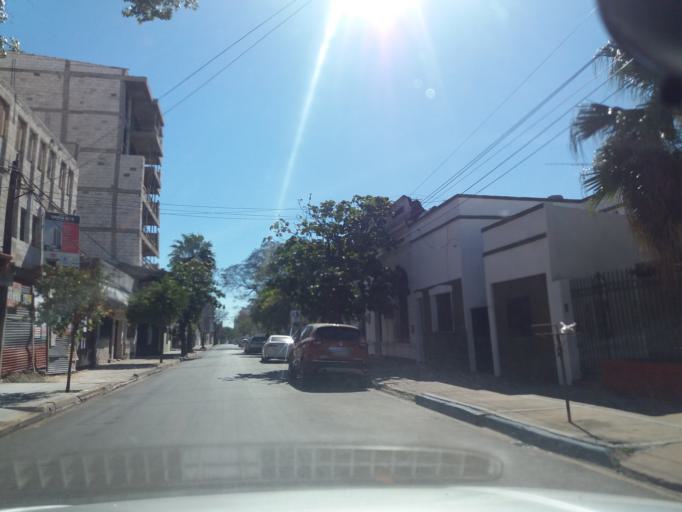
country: AR
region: Corrientes
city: Corrientes
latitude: -27.4736
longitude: -58.8410
